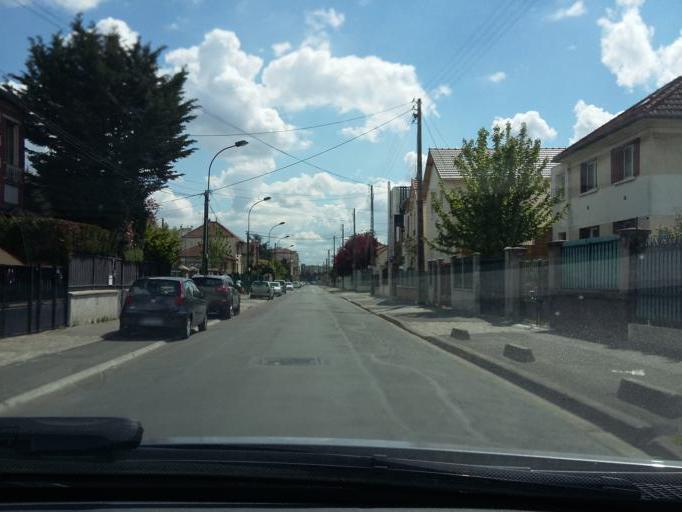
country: FR
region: Ile-de-France
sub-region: Departement du Val-d'Oise
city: Saint-Gratien
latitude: 48.9627
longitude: 2.2989
